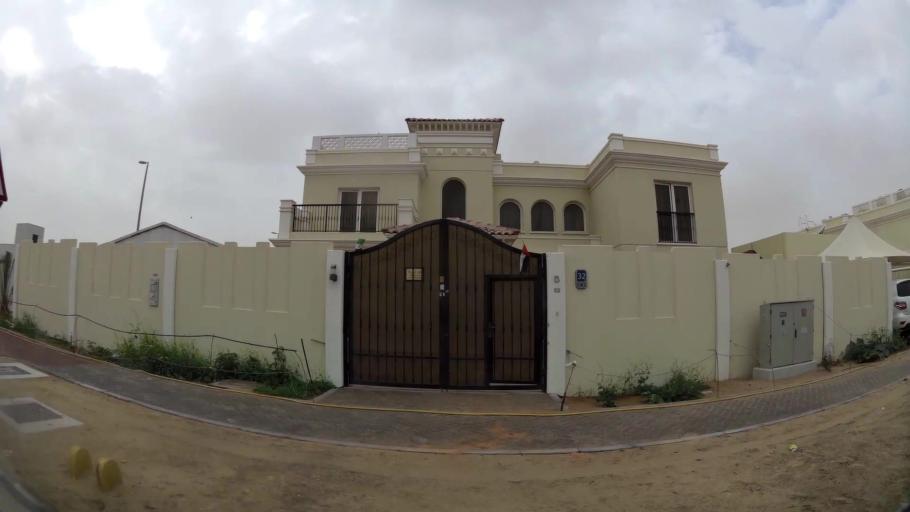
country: AE
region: Abu Dhabi
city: Abu Dhabi
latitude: 24.4471
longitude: 54.7146
